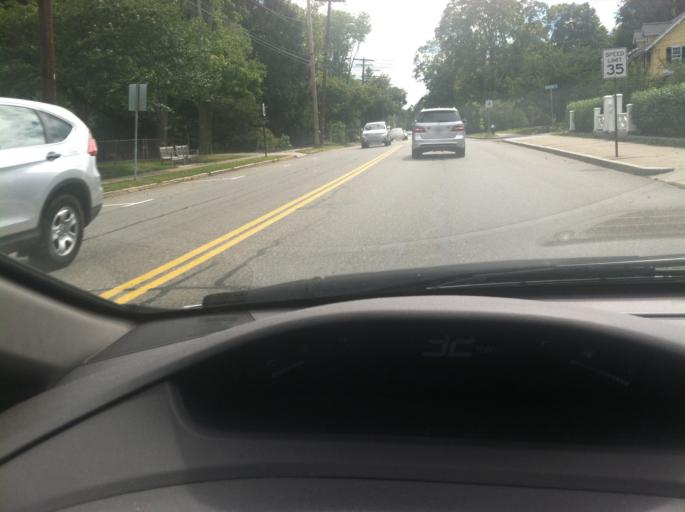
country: US
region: Massachusetts
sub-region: Middlesex County
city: Lexington
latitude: 42.4445
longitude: -71.2206
